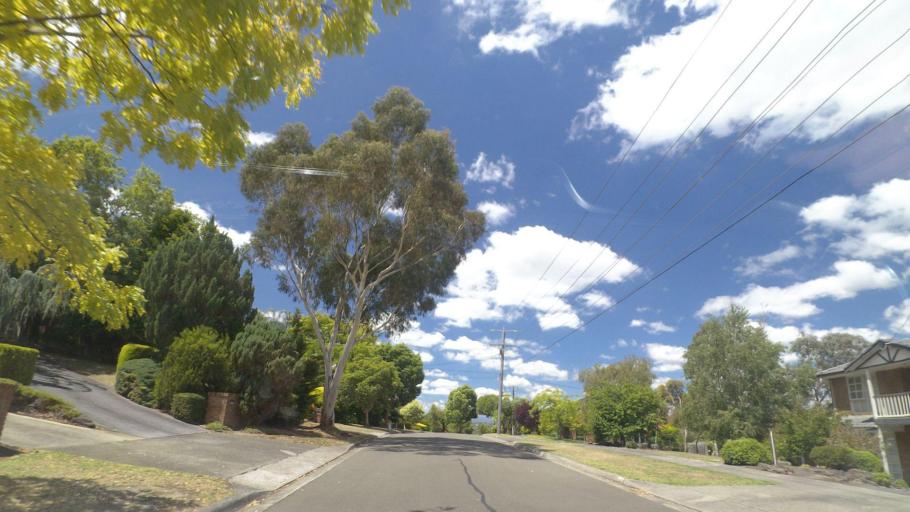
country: AU
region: Victoria
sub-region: Maroondah
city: Croydon Hills
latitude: -37.7635
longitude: 145.2766
